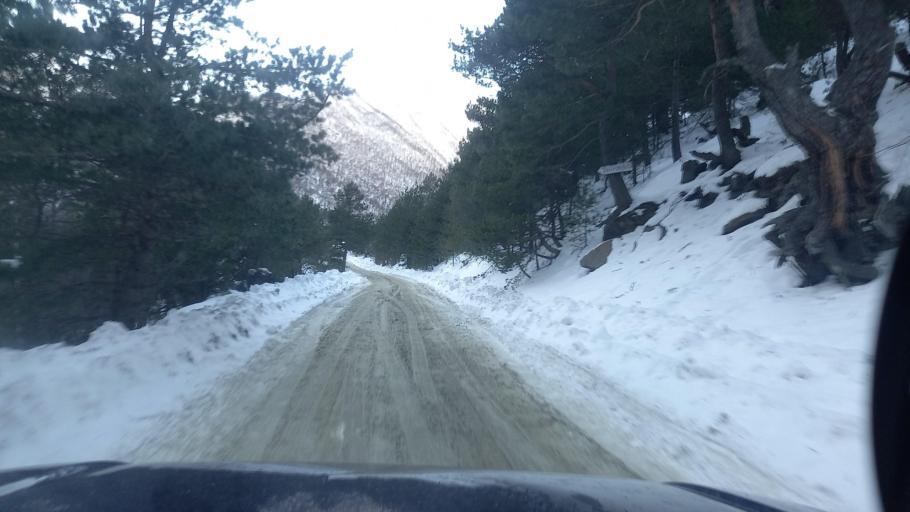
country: RU
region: Kabardino-Balkariya
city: Verkhnyaya Balkariya
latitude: 42.9022
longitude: 43.5886
